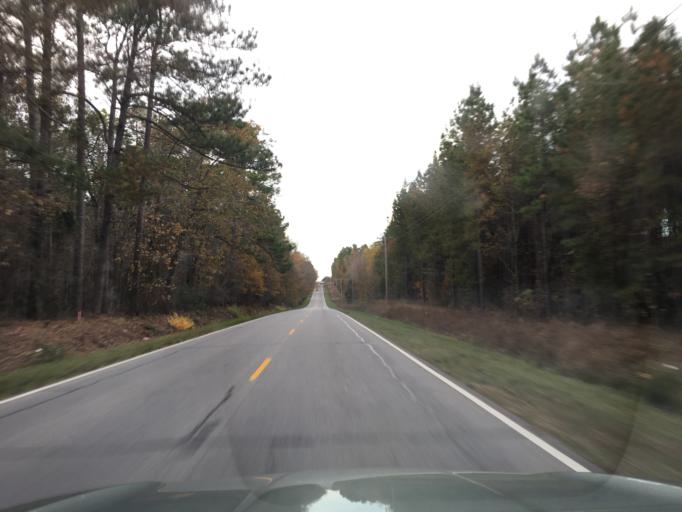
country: US
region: South Carolina
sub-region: Lexington County
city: Leesville
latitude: 33.8092
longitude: -81.4439
